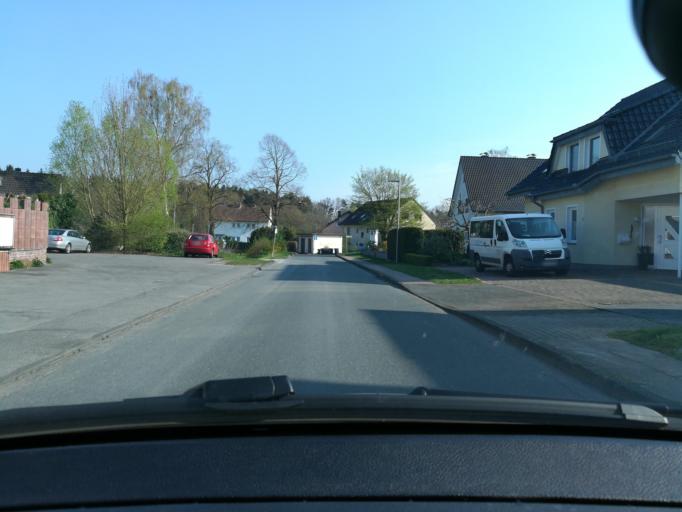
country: DE
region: North Rhine-Westphalia
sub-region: Regierungsbezirk Detmold
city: Oerlinghausen
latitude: 51.9297
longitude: 8.6049
